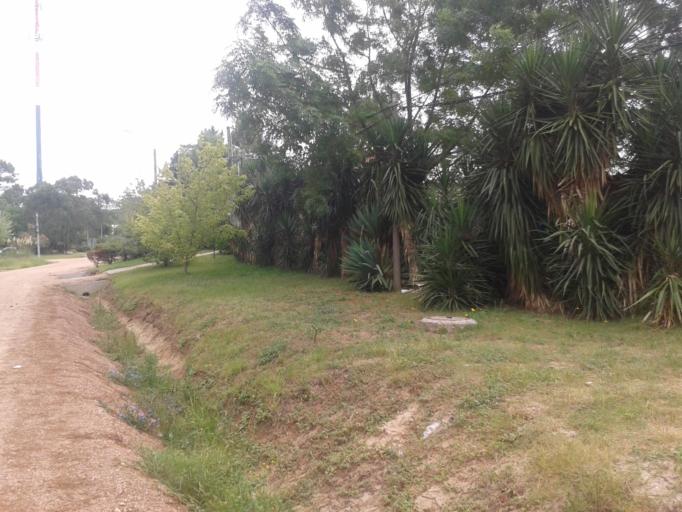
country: UY
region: Canelones
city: Pando
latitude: -34.8085
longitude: -55.9262
